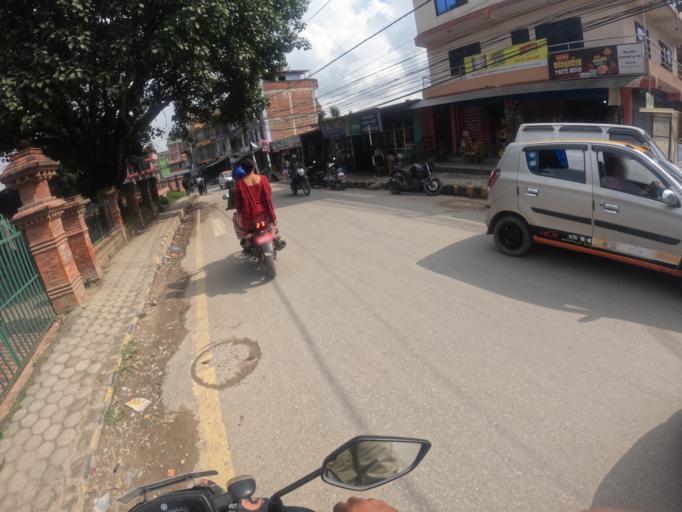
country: NP
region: Central Region
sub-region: Bagmati Zone
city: Bhaktapur
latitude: 27.6681
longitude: 85.3861
